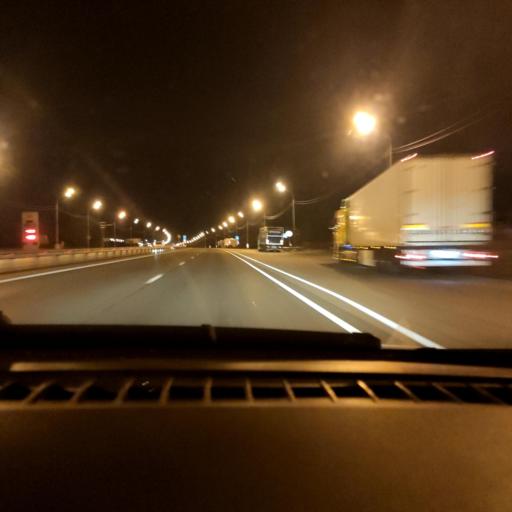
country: RU
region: Lipetsk
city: Khlevnoye
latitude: 52.1285
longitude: 39.1970
